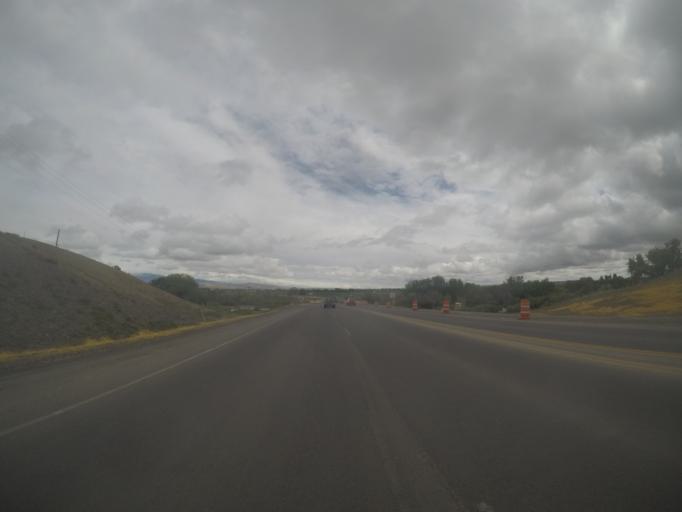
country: US
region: Wyoming
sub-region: Big Horn County
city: Lovell
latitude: 44.8399
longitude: -108.4352
